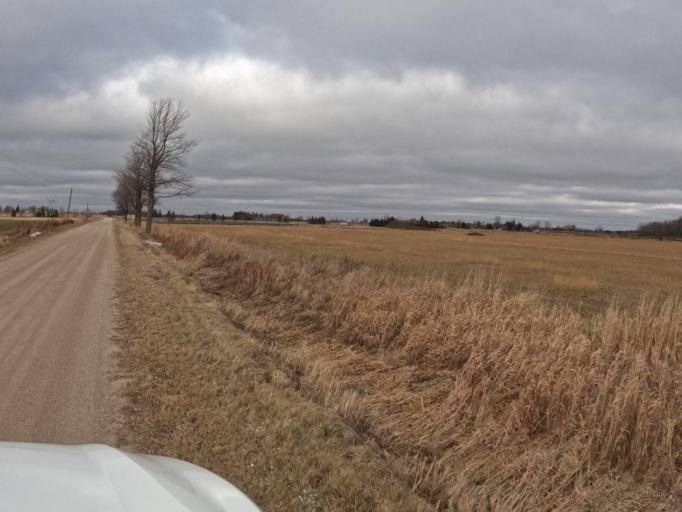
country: CA
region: Ontario
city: Shelburne
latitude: 43.8919
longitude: -80.3292
